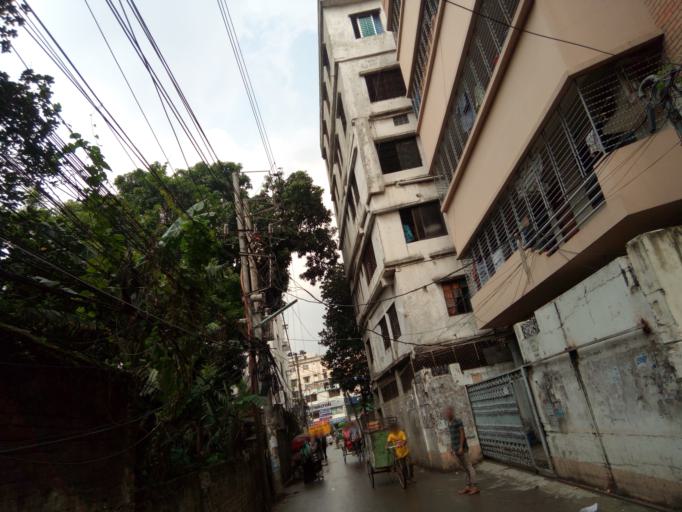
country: BD
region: Dhaka
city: Azimpur
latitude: 23.7620
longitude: 90.3883
